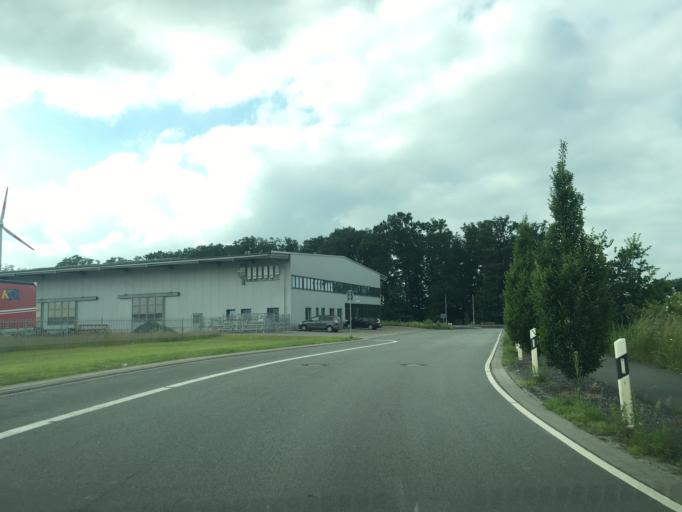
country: DE
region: North Rhine-Westphalia
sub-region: Regierungsbezirk Munster
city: Altenberge
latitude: 52.0758
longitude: 7.4514
